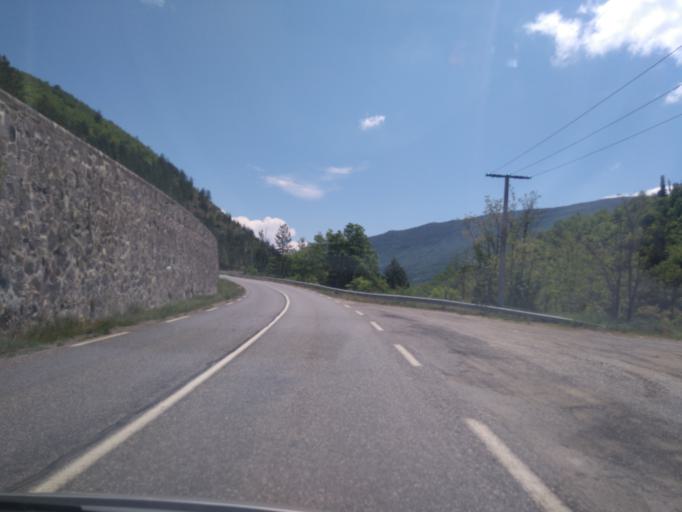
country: FR
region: Provence-Alpes-Cote d'Azur
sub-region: Departement des Hautes-Alpes
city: Laragne-Monteglin
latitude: 44.3421
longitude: 5.7759
